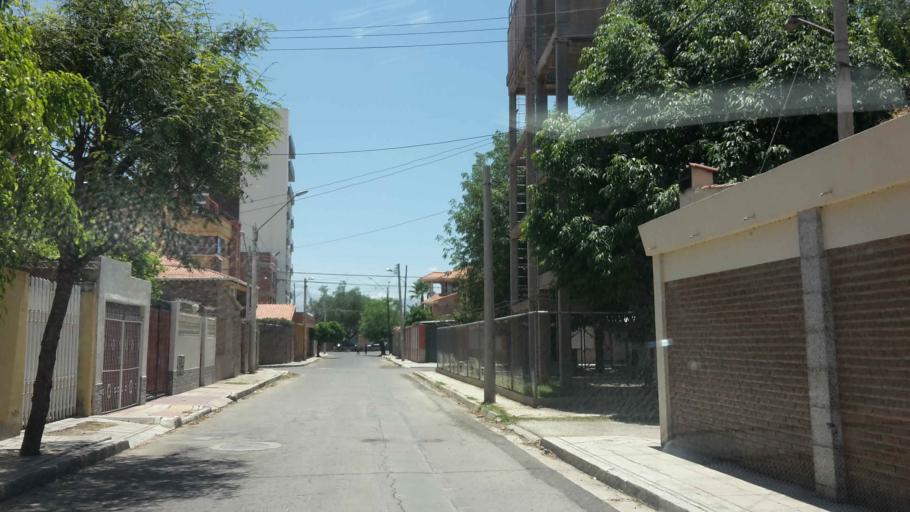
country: BO
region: Cochabamba
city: Cochabamba
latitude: -17.3852
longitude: -66.1870
